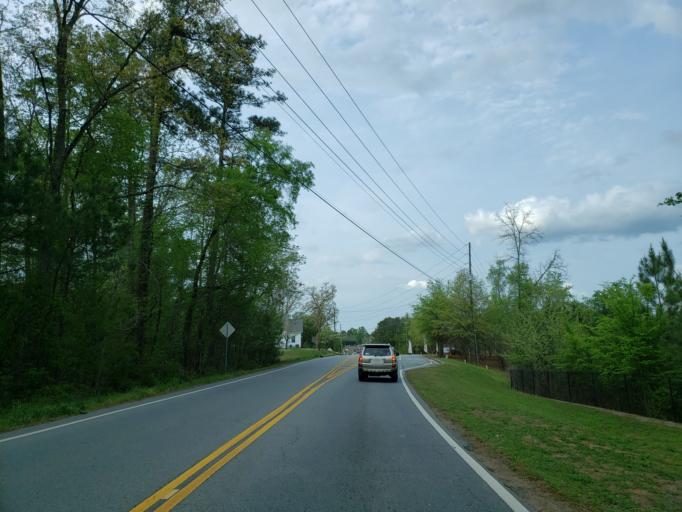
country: US
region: Georgia
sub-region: Cherokee County
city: Woodstock
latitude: 34.1148
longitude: -84.4709
